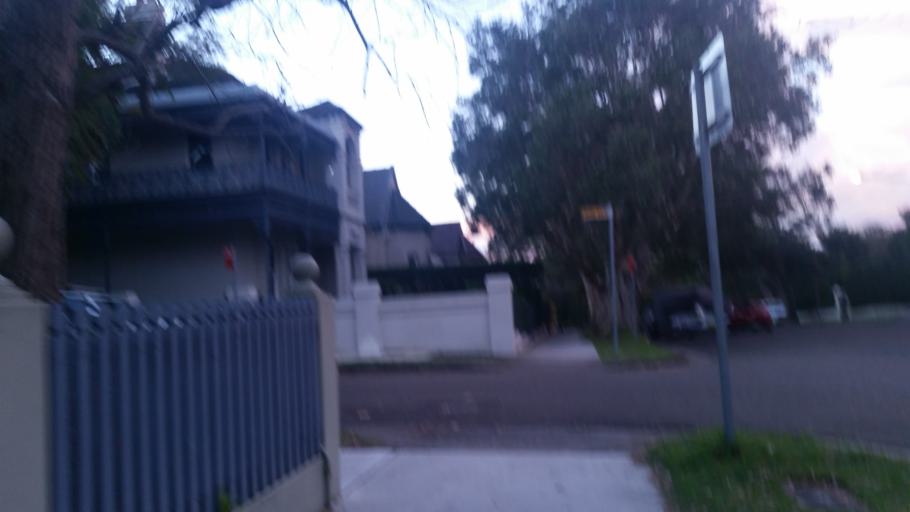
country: AU
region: New South Wales
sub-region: Waverley
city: Bronte
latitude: -33.9052
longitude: 151.2609
